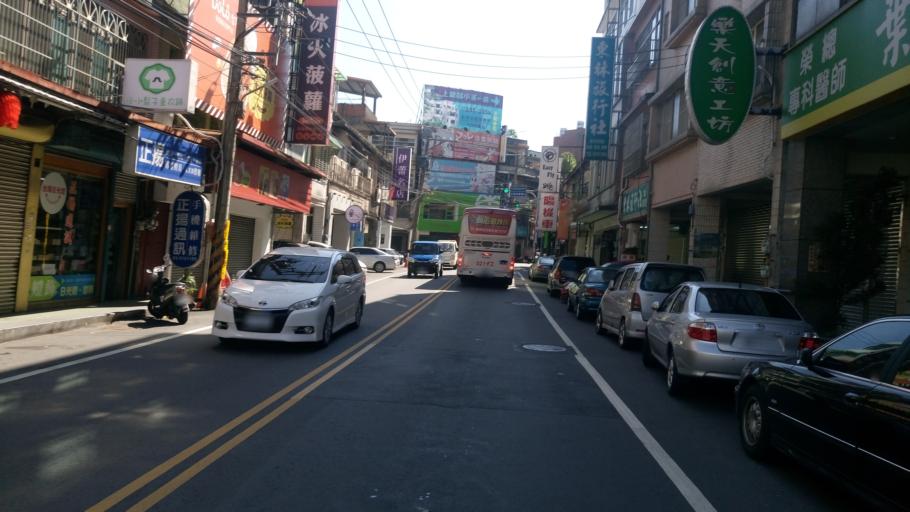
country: TW
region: Taiwan
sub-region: Hsinchu
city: Zhubei
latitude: 24.7372
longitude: 121.0881
